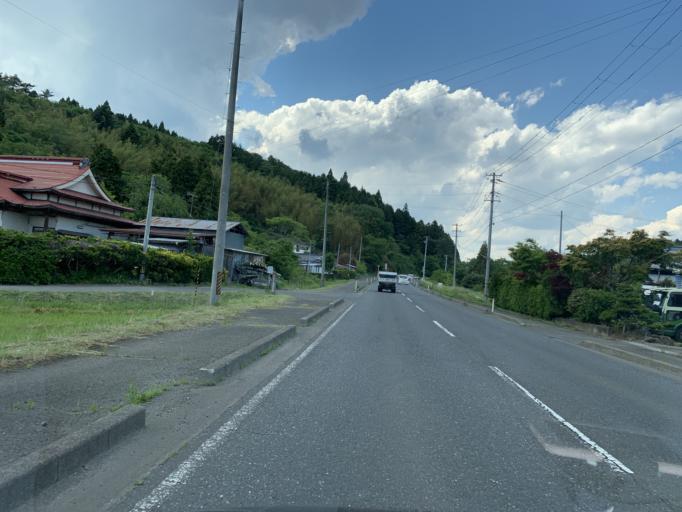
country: JP
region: Miyagi
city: Wakuya
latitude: 38.5507
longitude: 141.1408
